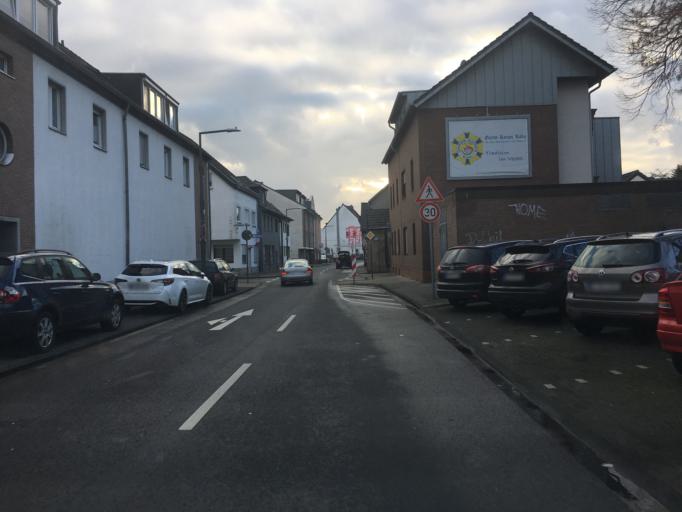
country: DE
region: North Rhine-Westphalia
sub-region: Regierungsbezirk Koln
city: Porz am Rhein
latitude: 50.8693
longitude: 7.0456
